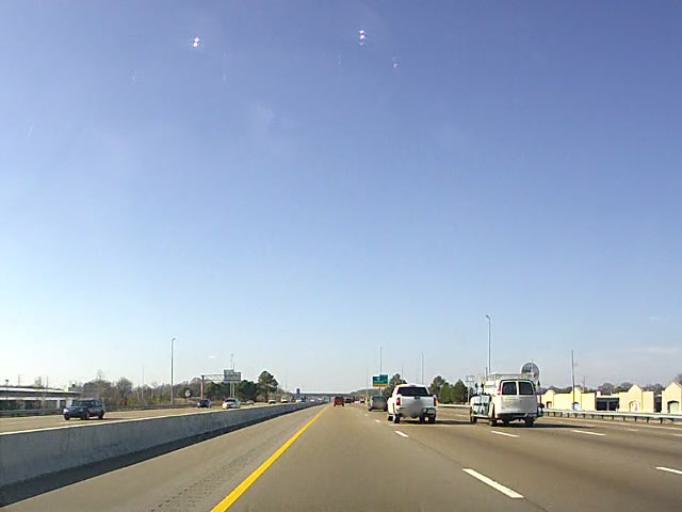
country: US
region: Tennessee
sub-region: Shelby County
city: Germantown
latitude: 35.0794
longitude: -89.9267
